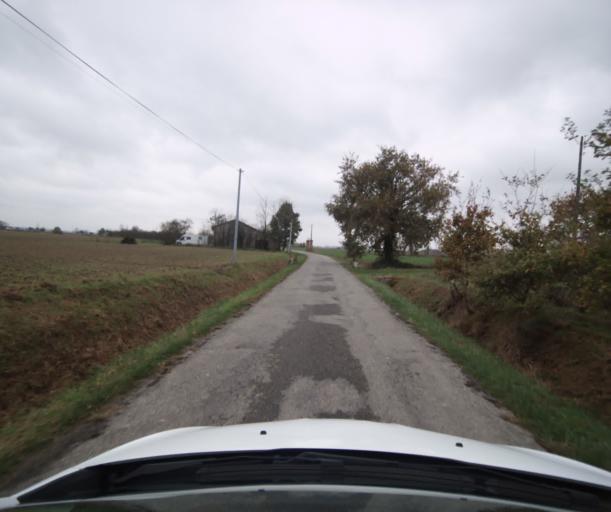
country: FR
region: Midi-Pyrenees
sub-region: Departement du Tarn-et-Garonne
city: Castelsarrasin
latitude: 44.0520
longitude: 1.1437
